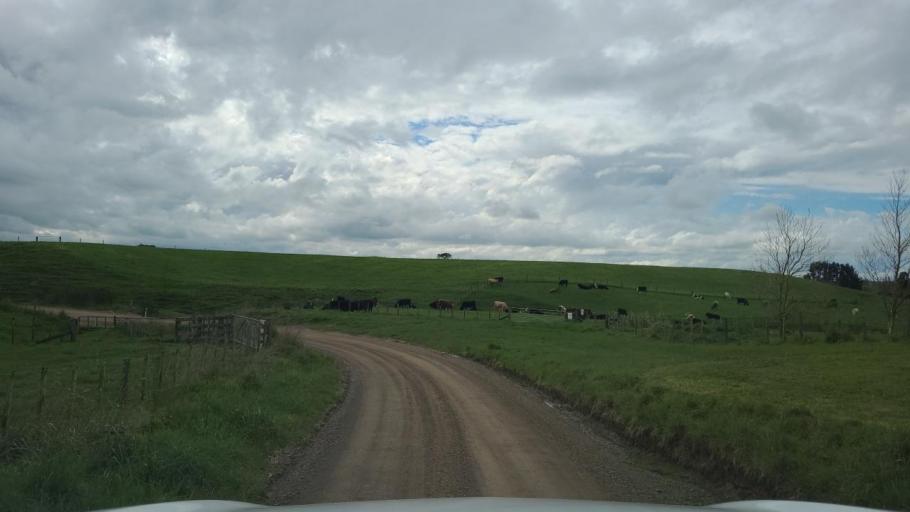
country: NZ
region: Wellington
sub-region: Masterton District
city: Masterton
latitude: -41.1100
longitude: 175.5489
